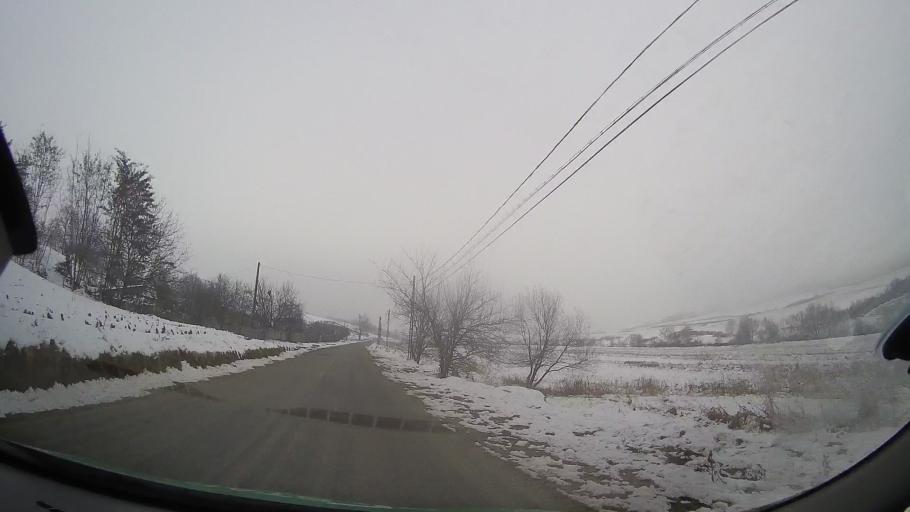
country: RO
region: Bacau
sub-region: Comuna Vultureni
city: Vultureni
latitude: 46.3196
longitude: 27.2928
